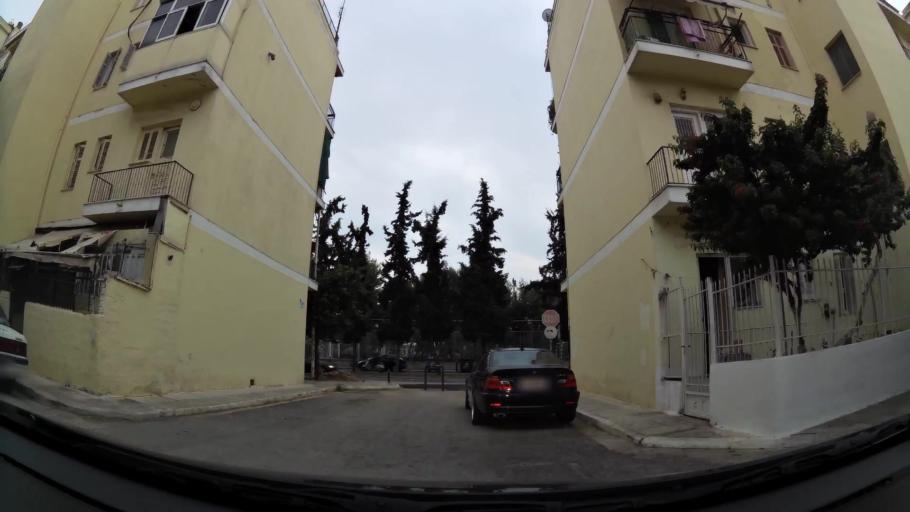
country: GR
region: Attica
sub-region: Nomos Piraios
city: Agios Ioannis Rentis
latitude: 37.9660
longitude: 23.6661
